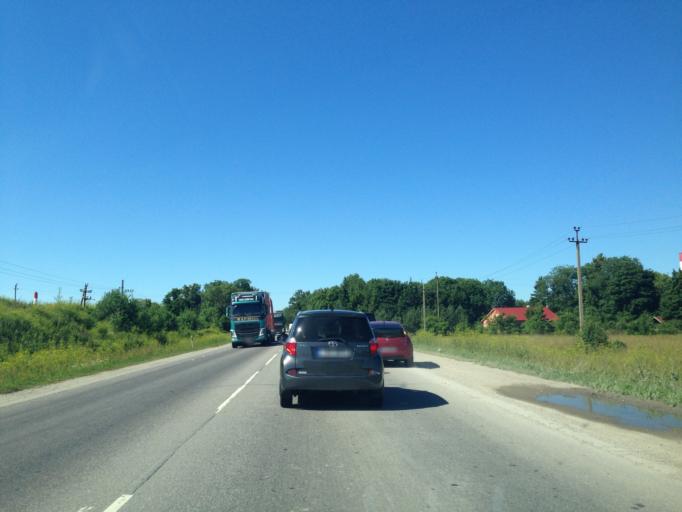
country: EE
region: Harju
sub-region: Joelaehtme vald
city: Loo
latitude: 59.4319
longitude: 24.9188
